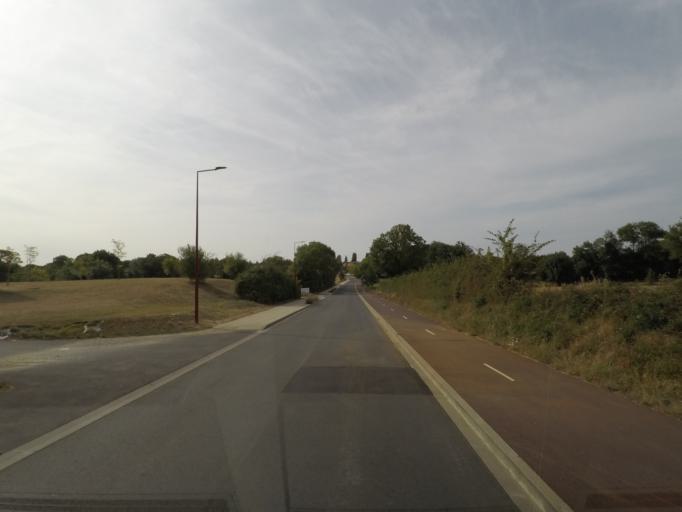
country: FR
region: Poitou-Charentes
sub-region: Departement des Deux-Sevres
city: Melle
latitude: 46.2284
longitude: -0.1288
